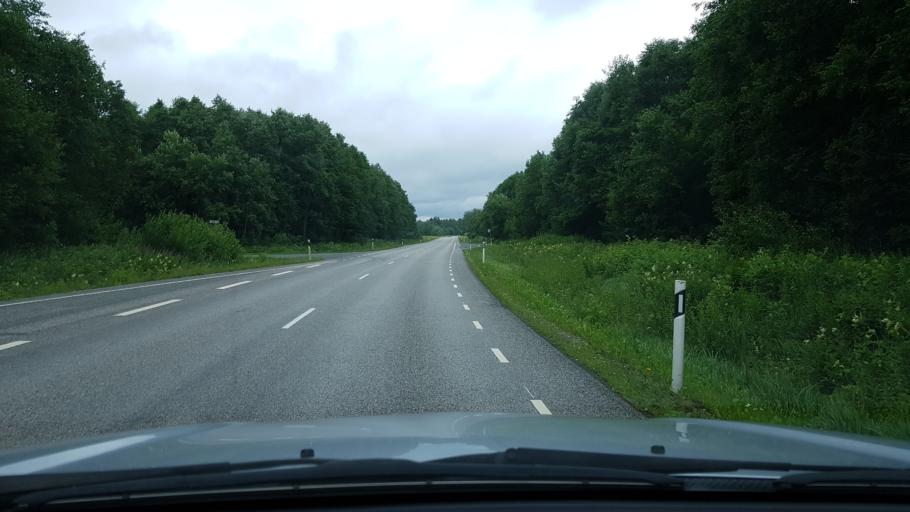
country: EE
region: Ida-Virumaa
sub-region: Narva-Joesuu linn
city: Narva-Joesuu
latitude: 59.3445
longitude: 27.9332
